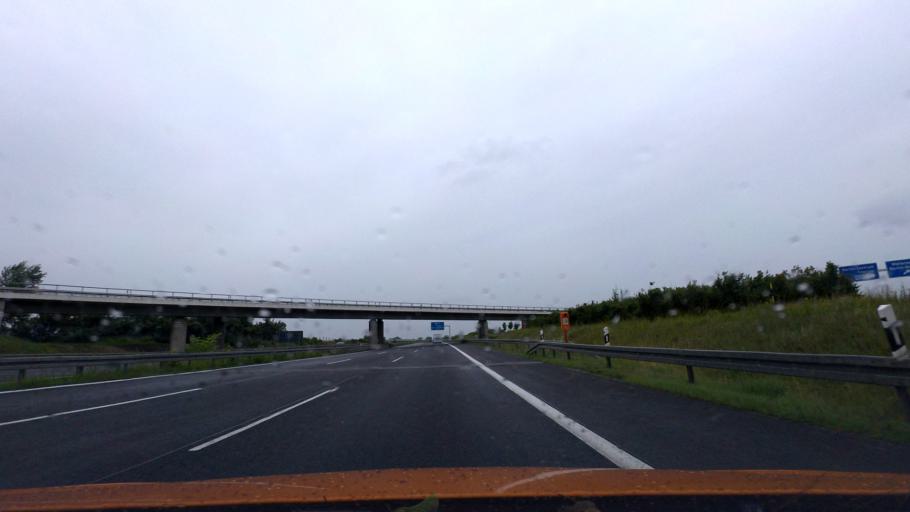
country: DE
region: Brandenburg
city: Schulzendorf
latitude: 52.3637
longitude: 13.5484
